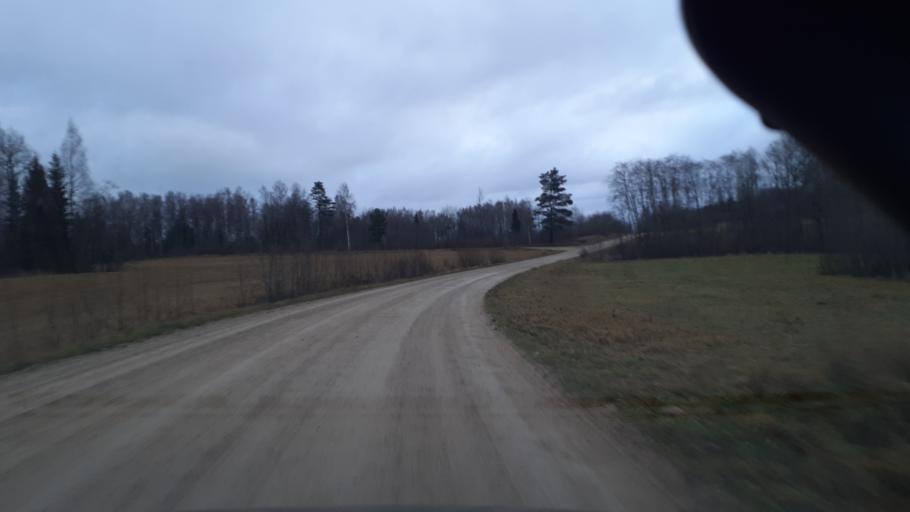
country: LV
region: Alsunga
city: Alsunga
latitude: 56.8875
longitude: 21.6949
